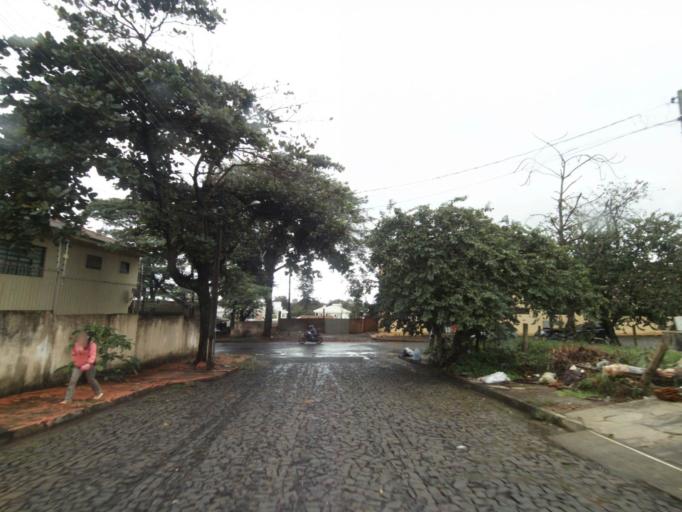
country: PY
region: Alto Parana
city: Ciudad del Este
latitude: -25.5148
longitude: -54.5796
